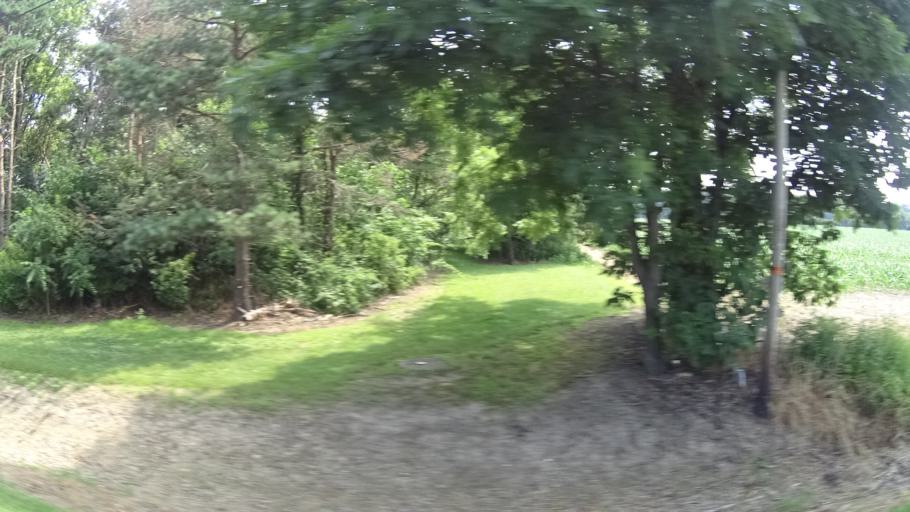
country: US
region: Ohio
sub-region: Lorain County
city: Vermilion
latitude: 41.3975
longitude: -82.4063
